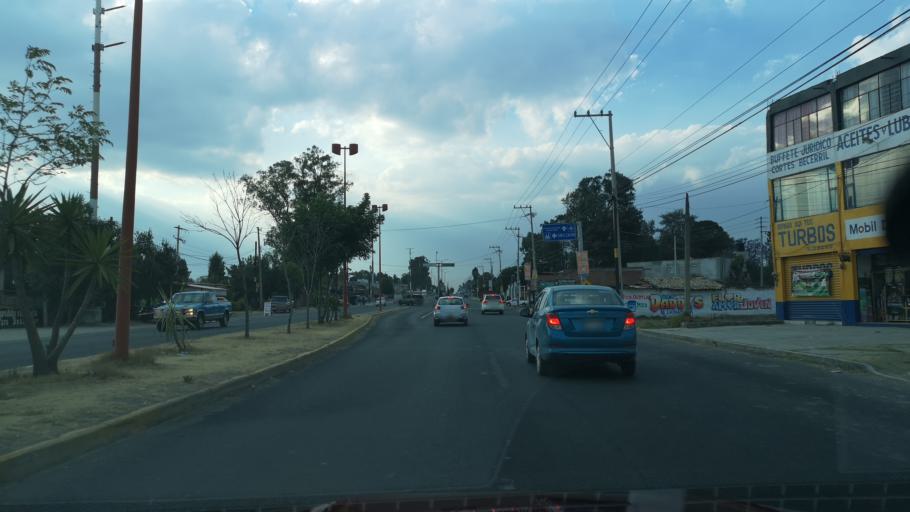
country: MX
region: Puebla
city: Cuanala
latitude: 19.1012
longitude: -98.3458
